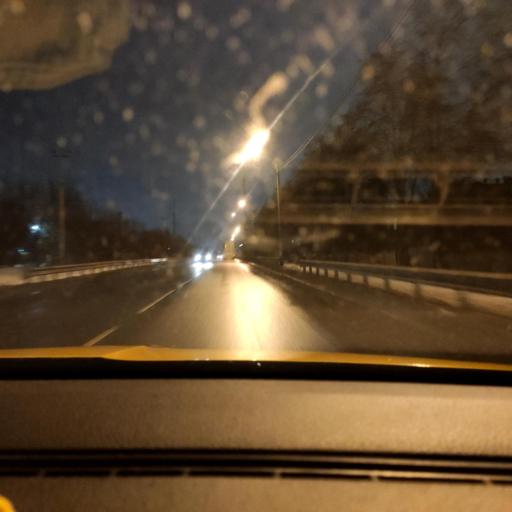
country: RU
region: Moskovskaya
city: Mosrentgen
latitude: 55.6129
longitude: 37.4600
